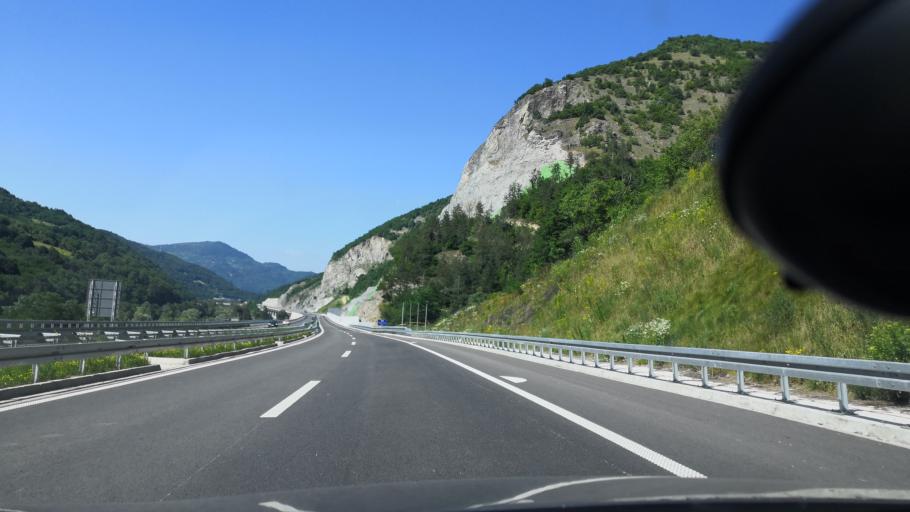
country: RS
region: Central Serbia
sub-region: Pcinjski Okrug
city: Vladicin Han
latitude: 42.7503
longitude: 22.0827
